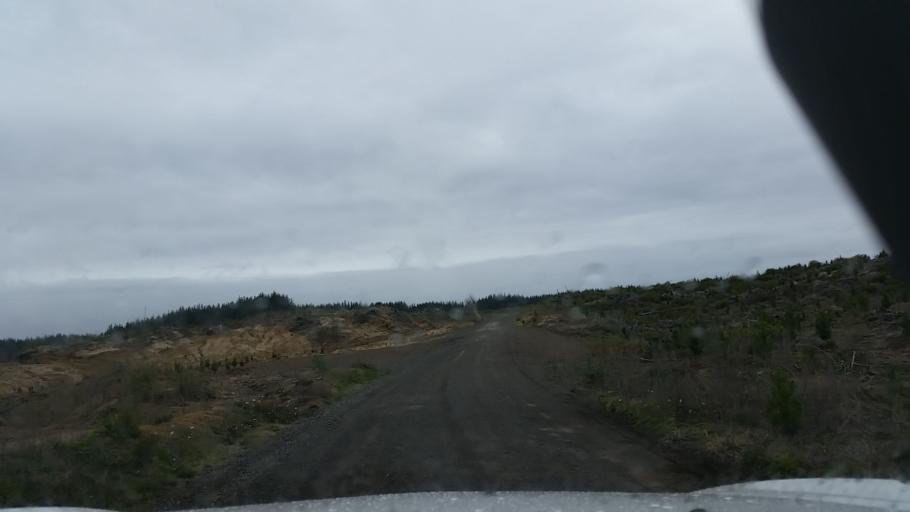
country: NZ
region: Bay of Plenty
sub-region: Kawerau District
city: Kawerau
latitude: -37.9991
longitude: 176.5448
